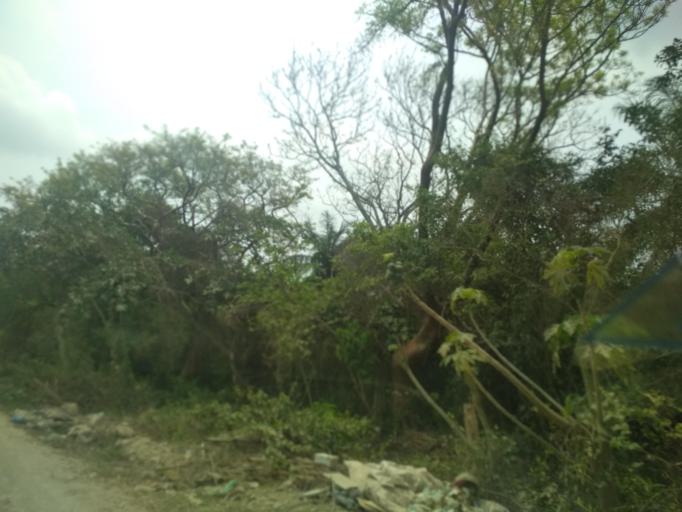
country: MX
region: Veracruz
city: Paso del Toro
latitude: 19.0403
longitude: -96.1511
